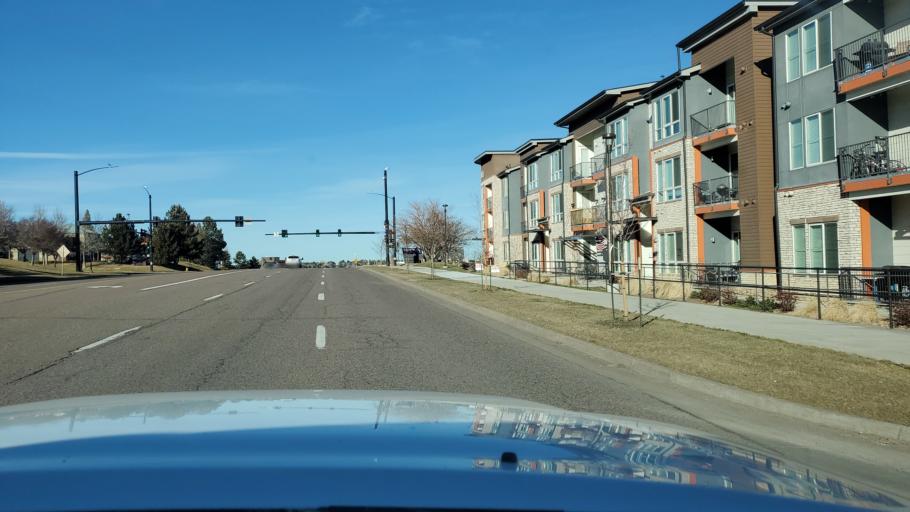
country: US
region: Colorado
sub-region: Arapahoe County
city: Centennial
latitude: 39.5833
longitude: -104.8667
